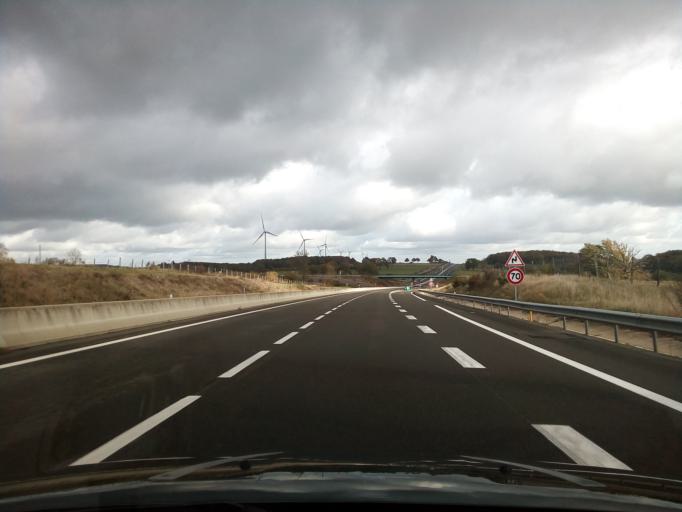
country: FR
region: Auvergne
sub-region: Departement de l'Allier
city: Huriel
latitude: 46.3036
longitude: 2.4432
